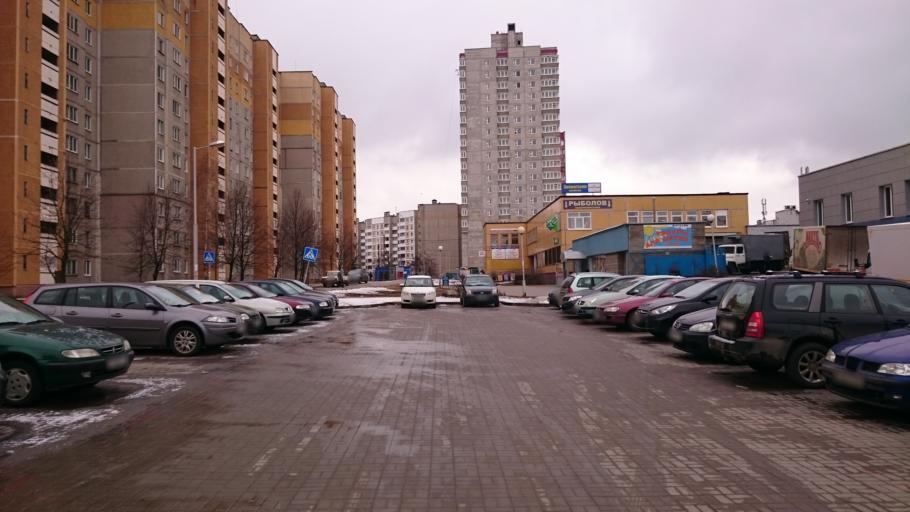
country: BY
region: Minsk
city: Borovlyany
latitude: 53.9382
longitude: 27.6865
